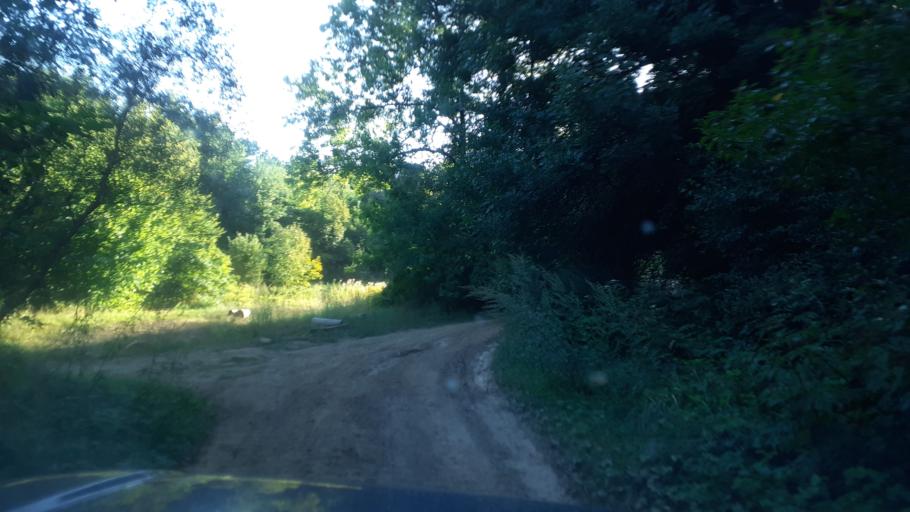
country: RU
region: Krasnodarskiy
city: Pshada
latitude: 44.6556
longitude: 38.4404
